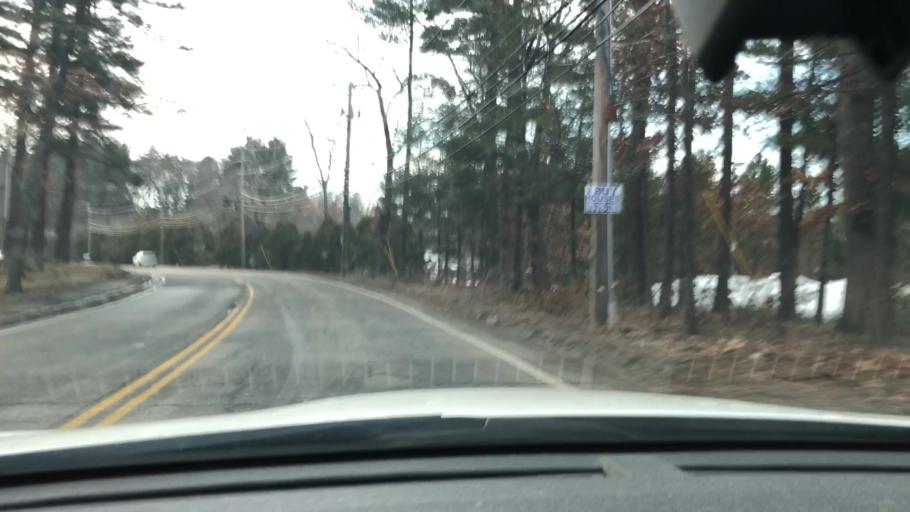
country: US
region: Massachusetts
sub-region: Middlesex County
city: Chelmsford
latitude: 42.5976
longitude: -71.3311
